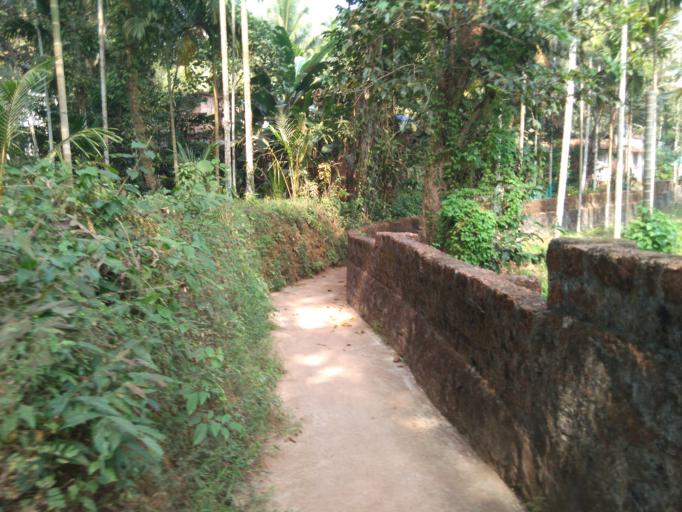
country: IN
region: Kerala
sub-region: Kozhikode
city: Kunnamangalam
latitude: 11.2896
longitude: 75.8307
